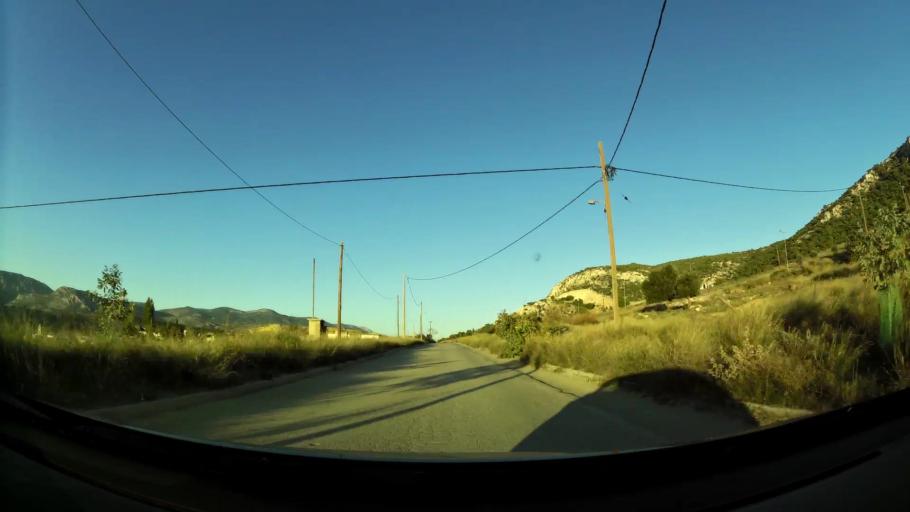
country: GR
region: Attica
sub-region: Nomarchia Athinas
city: Chaidari
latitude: 38.0448
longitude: 23.6430
